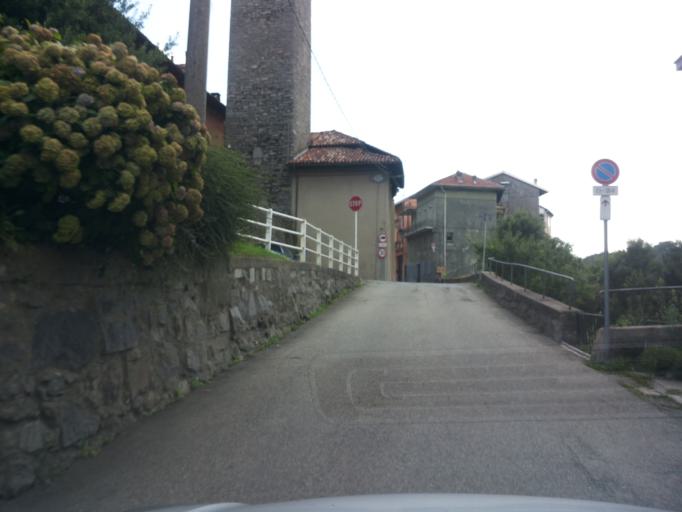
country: IT
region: Piedmont
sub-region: Provincia di Biella
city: Sagliano Micca
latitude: 45.6243
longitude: 8.0440
